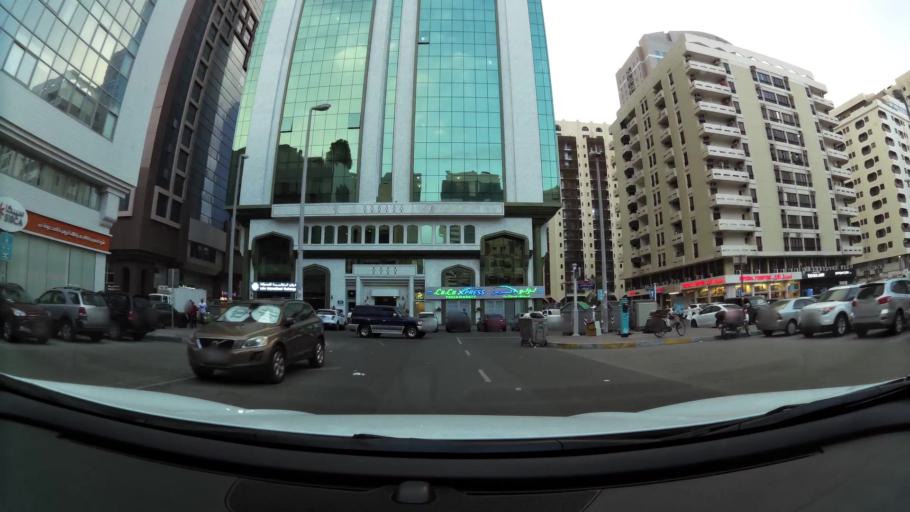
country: AE
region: Abu Dhabi
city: Abu Dhabi
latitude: 24.4936
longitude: 54.3704
